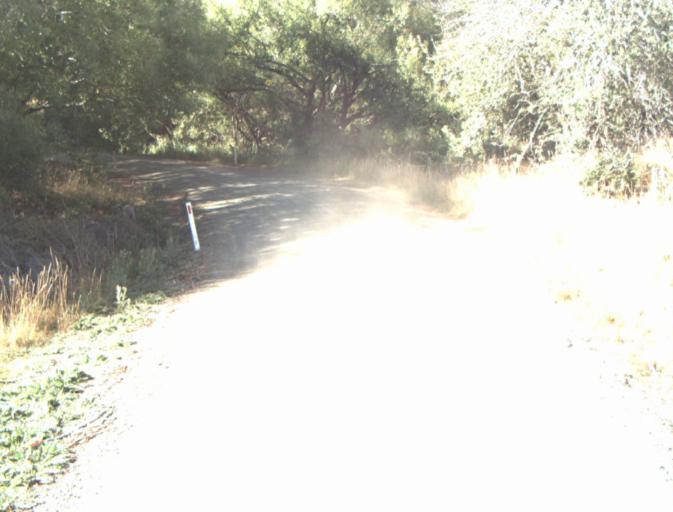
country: AU
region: Tasmania
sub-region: Dorset
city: Bridport
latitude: -41.1481
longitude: 147.2224
